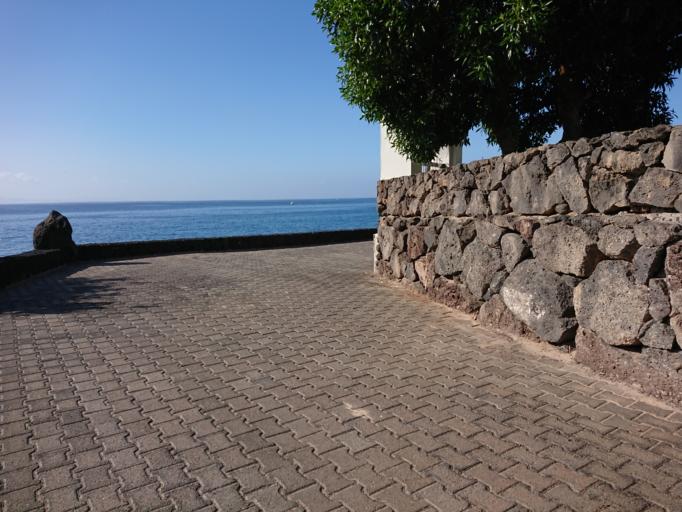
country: ES
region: Canary Islands
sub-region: Provincia de Las Palmas
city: Playa Blanca
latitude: 28.8618
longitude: -13.8515
